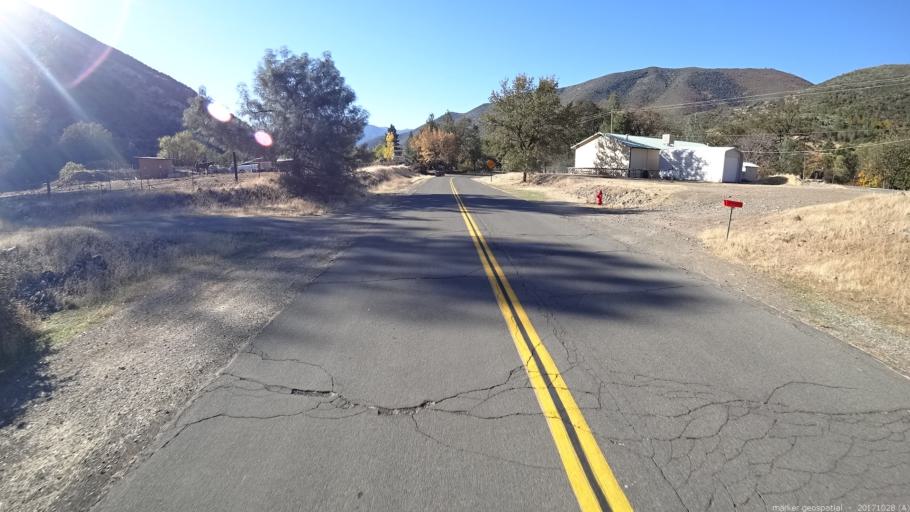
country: US
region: California
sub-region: Trinity County
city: Lewiston
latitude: 40.7062
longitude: -122.6350
